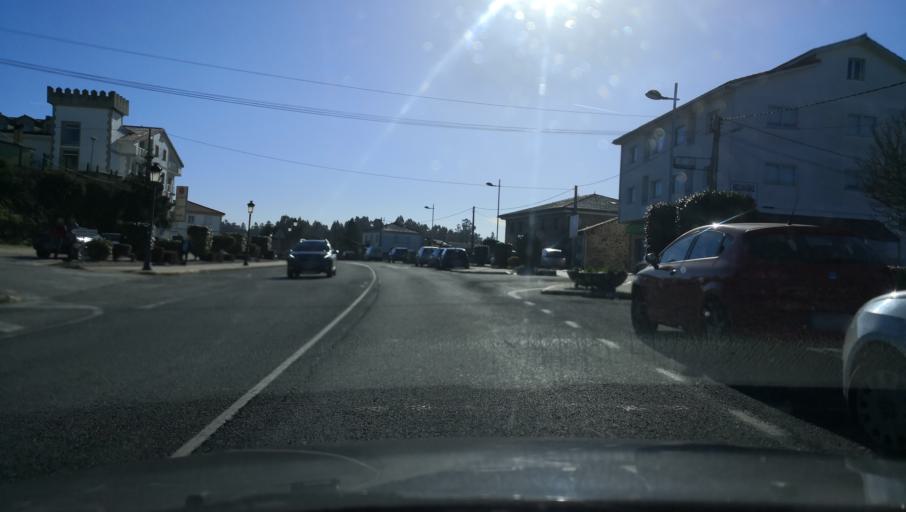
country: ES
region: Galicia
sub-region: Provincia da Coruna
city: Vedra
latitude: 42.7964
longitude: -8.4683
